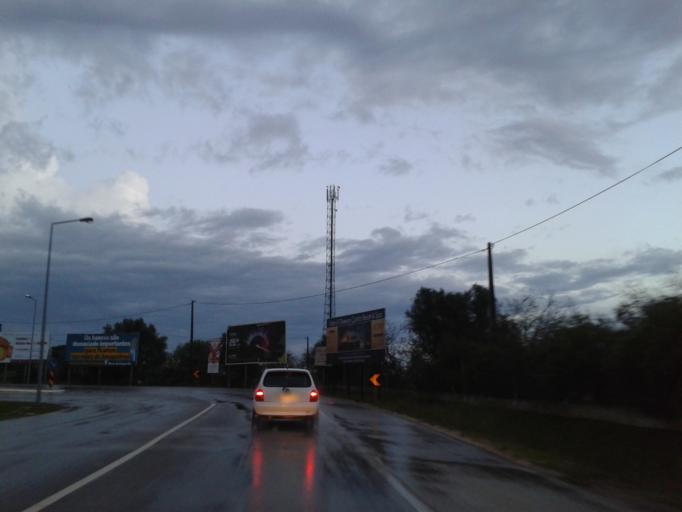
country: PT
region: Faro
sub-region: Lagoa
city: Lagoa
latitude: 37.1349
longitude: -8.4601
